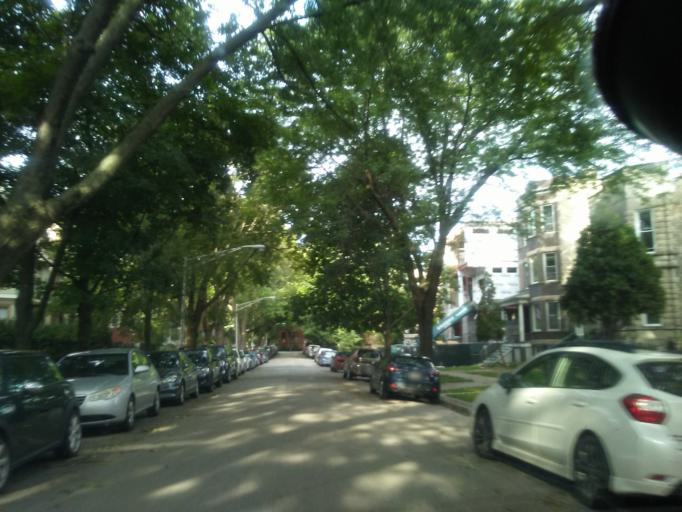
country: US
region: Illinois
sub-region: Cook County
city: Evanston
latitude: 41.9746
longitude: -87.6627
